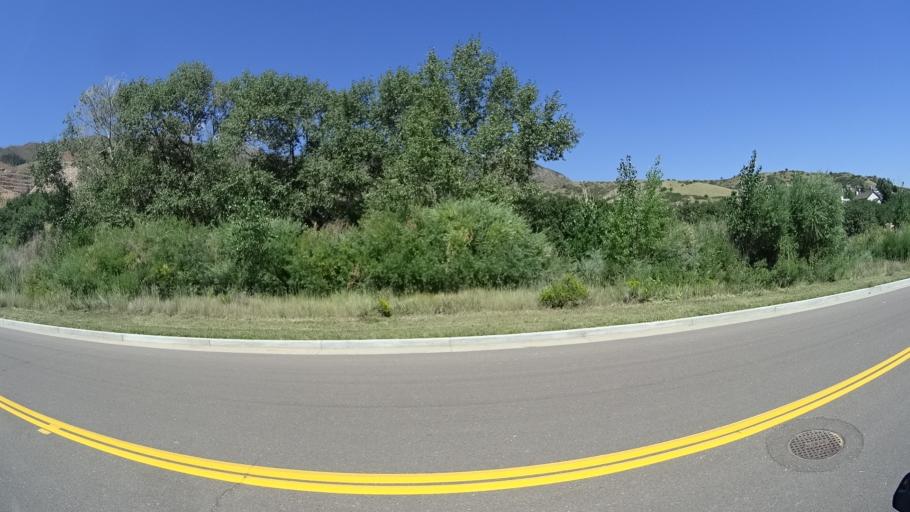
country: US
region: Colorado
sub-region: El Paso County
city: Air Force Academy
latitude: 38.9353
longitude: -104.8804
